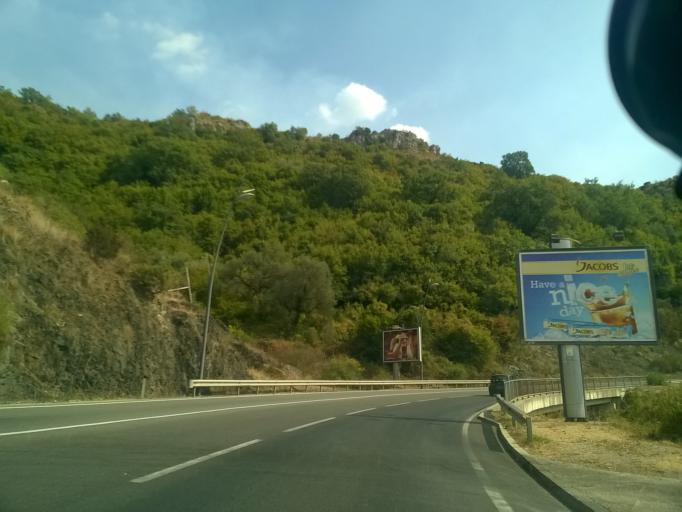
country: ME
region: Budva
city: Budva
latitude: 42.2807
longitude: 18.8850
